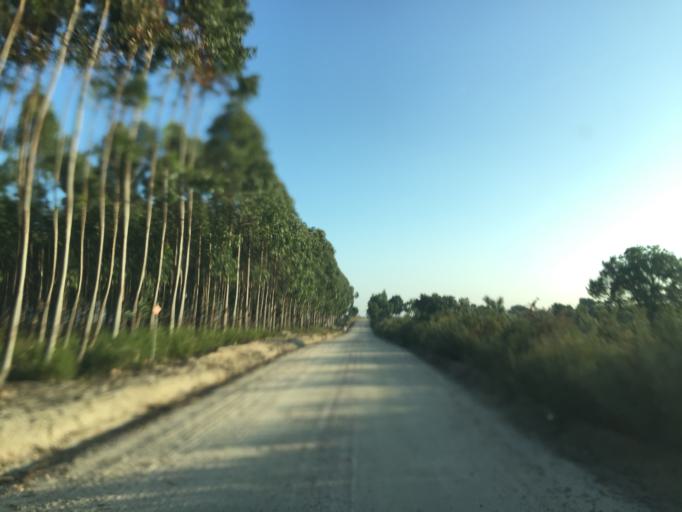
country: PT
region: Portalegre
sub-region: Ponte de Sor
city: Santo Andre
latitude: 39.1071
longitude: -8.3438
